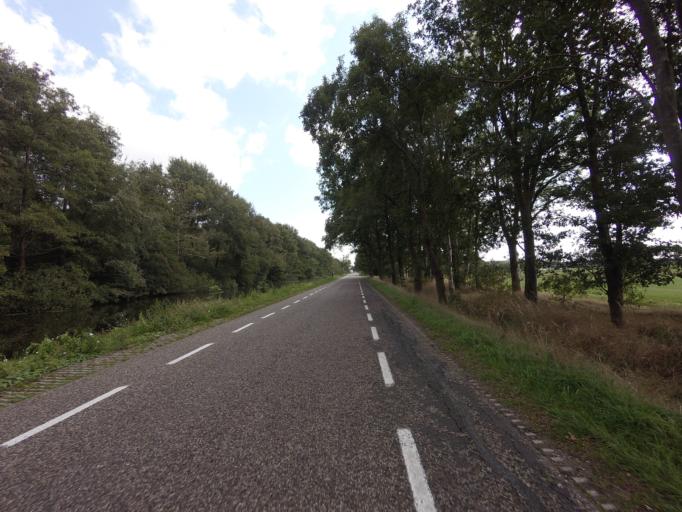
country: NL
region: Drenthe
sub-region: Gemeente Westerveld
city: Dwingeloo
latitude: 52.8697
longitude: 6.4464
